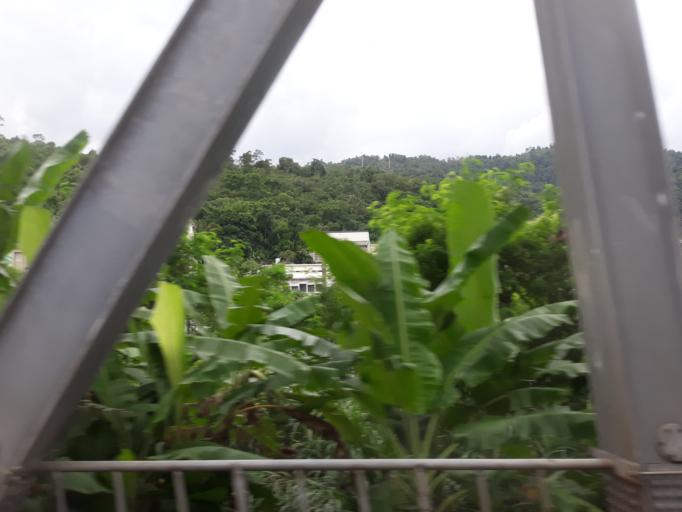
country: TW
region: Taiwan
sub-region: Yilan
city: Yilan
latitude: 24.6163
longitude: 121.8112
